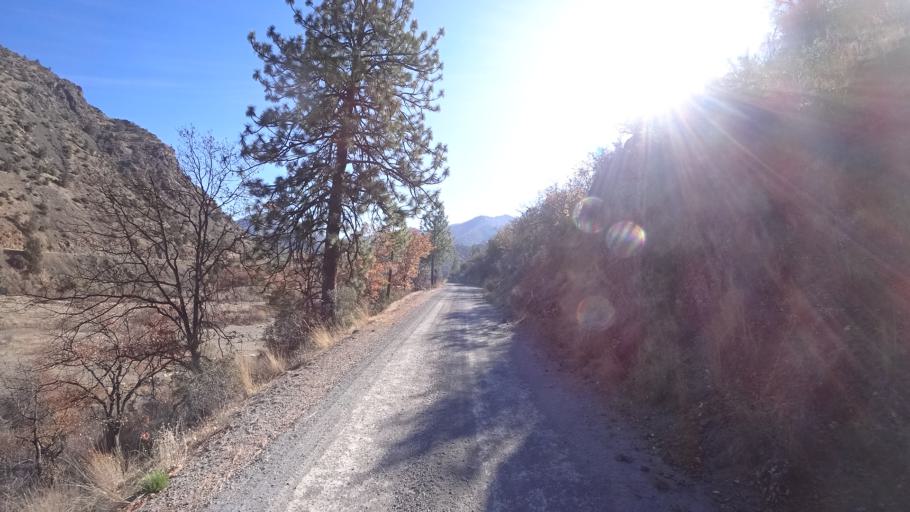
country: US
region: California
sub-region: Siskiyou County
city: Yreka
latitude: 41.8371
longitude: -122.6706
